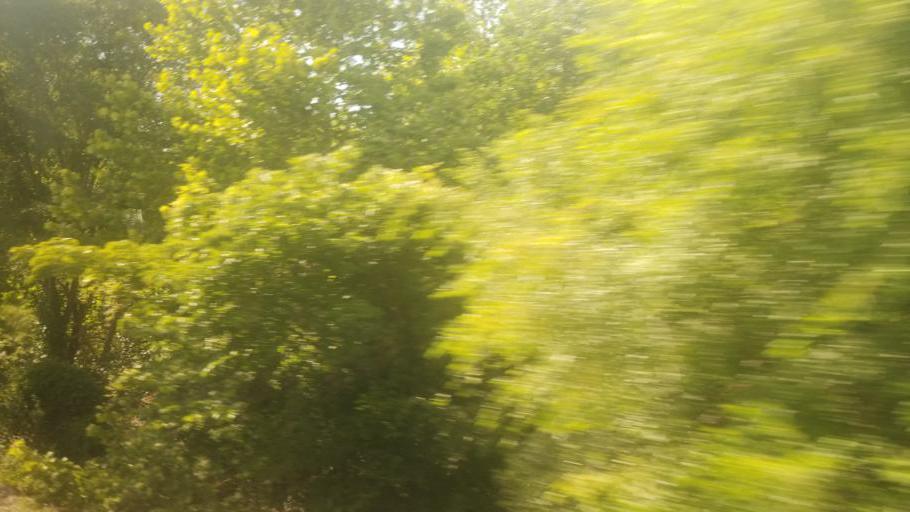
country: US
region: Kansas
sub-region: Wyandotte County
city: Edwardsville
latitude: 39.0501
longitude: -94.8426
